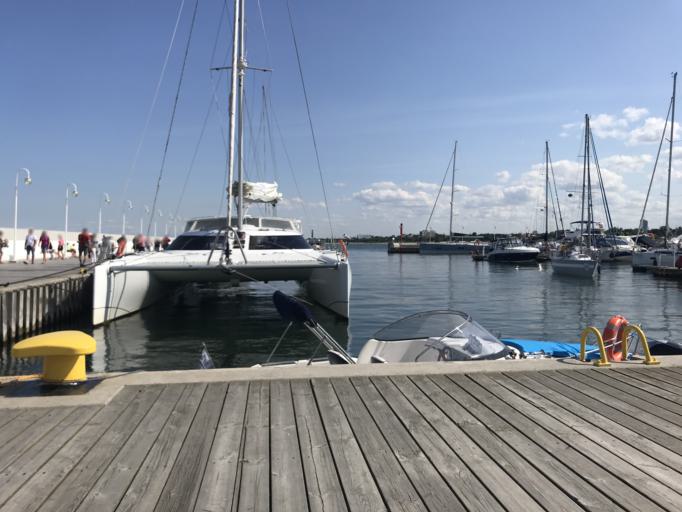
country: PL
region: Pomeranian Voivodeship
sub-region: Sopot
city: Sopot
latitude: 54.4483
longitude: 18.5781
